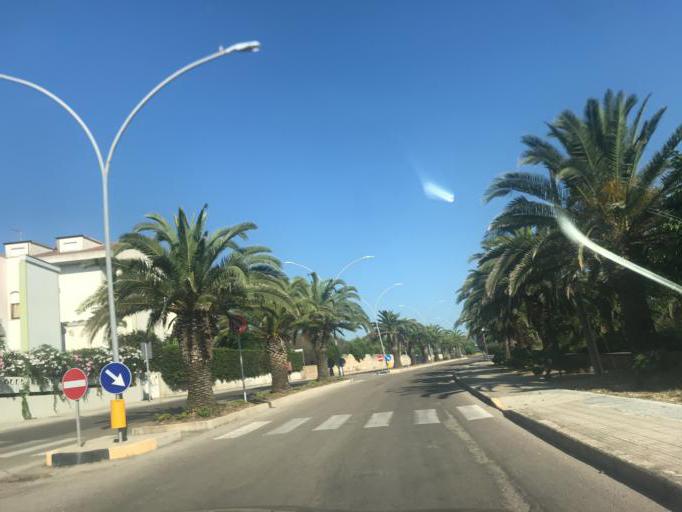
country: IT
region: Sardinia
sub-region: Provincia di Sassari
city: Alghero
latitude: 40.5512
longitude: 8.3279
